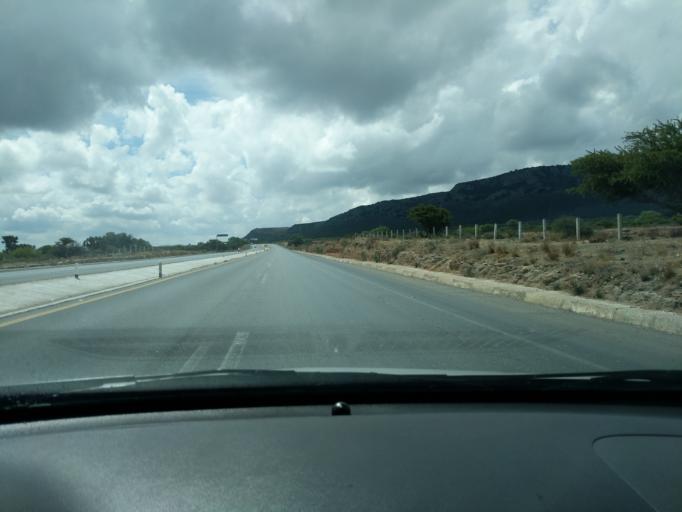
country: MX
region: Zacatecas
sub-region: Pinos
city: Santiago
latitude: 22.4042
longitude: -101.3860
